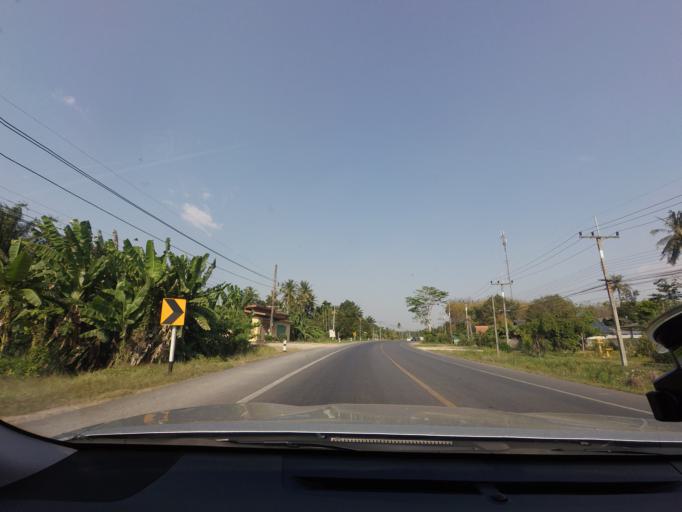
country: TH
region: Surat Thani
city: Phrasaeng
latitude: 8.5685
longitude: 99.1923
